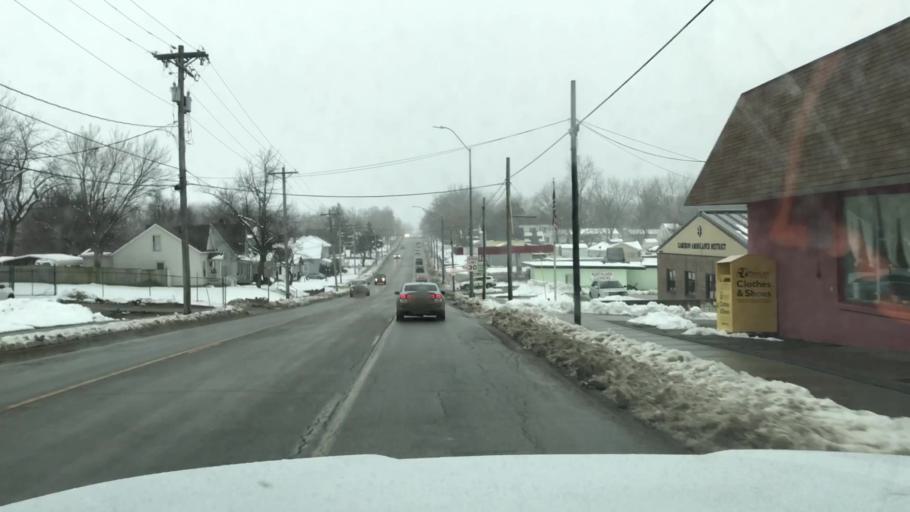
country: US
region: Missouri
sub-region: Clinton County
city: Cameron
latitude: 39.7385
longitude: -94.2360
